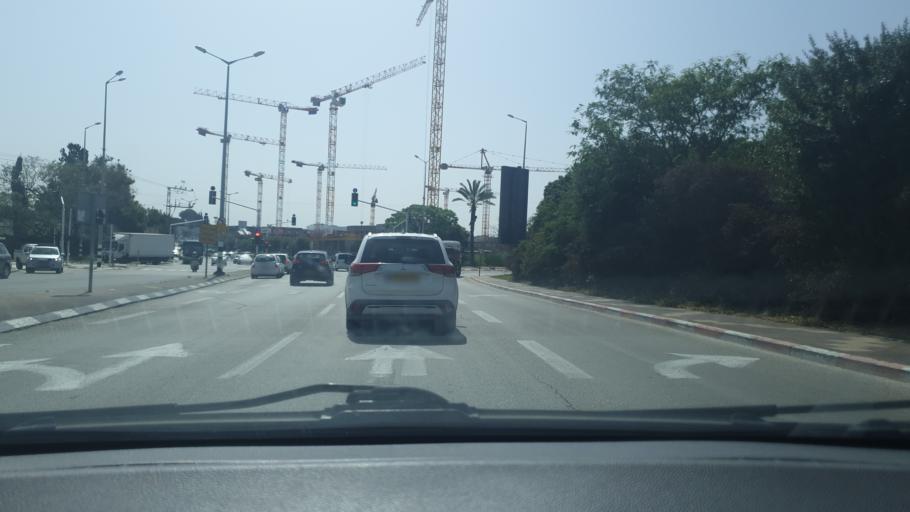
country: IL
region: Tel Aviv
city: Giv`at Shemu'el
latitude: 32.0525
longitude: 34.8371
